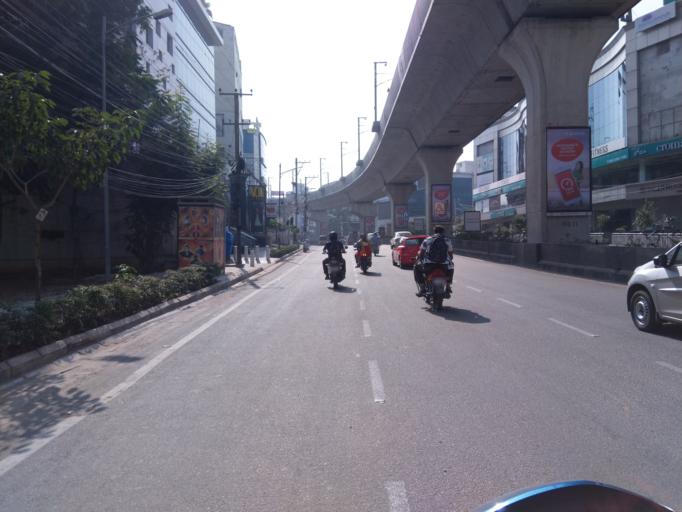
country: IN
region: Telangana
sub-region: Rangareddi
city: Kukatpalli
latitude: 17.4366
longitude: 78.4010
